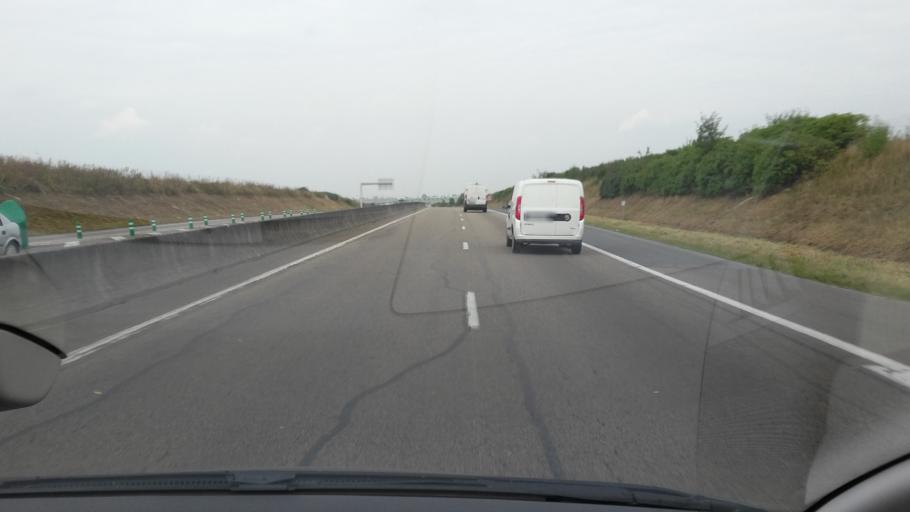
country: FR
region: Champagne-Ardenne
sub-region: Departement de la Marne
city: Cernay-les-Reims
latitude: 49.2442
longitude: 4.0808
